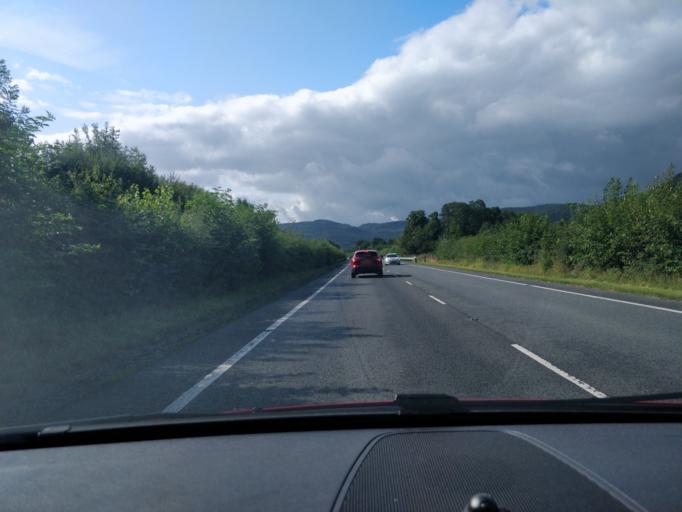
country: GB
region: Wales
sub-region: Conwy
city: Llanrwst
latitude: 53.1619
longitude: -3.8113
